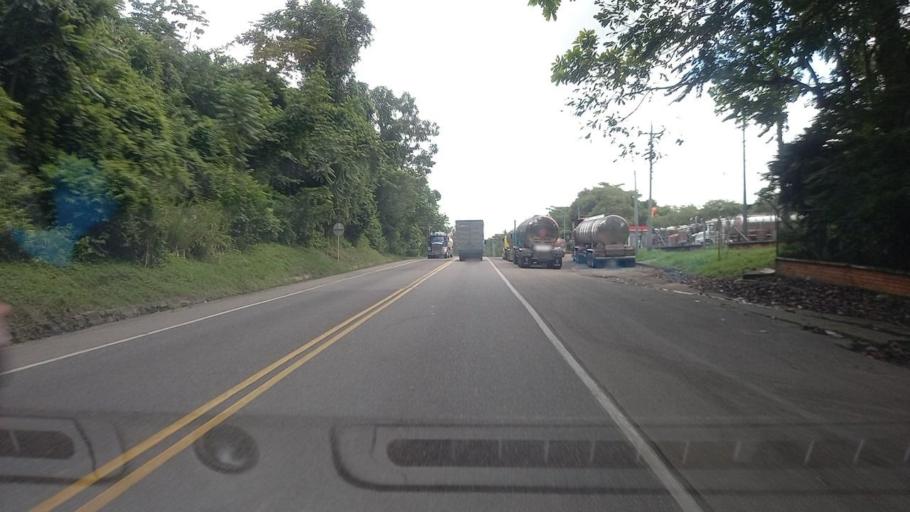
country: CO
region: Santander
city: Sabana de Torres
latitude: 7.1280
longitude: -73.5718
